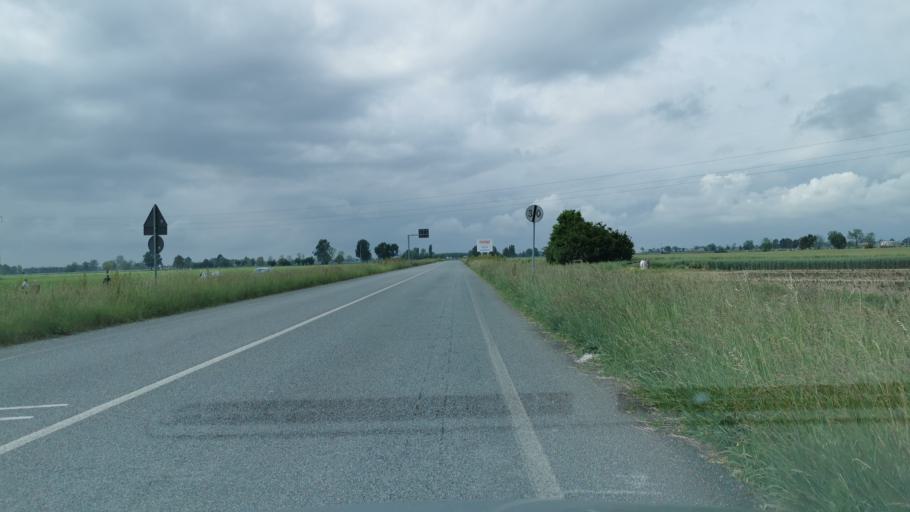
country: IT
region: Piedmont
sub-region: Provincia di Cuneo
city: Racconigi
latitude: 44.7623
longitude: 7.6972
